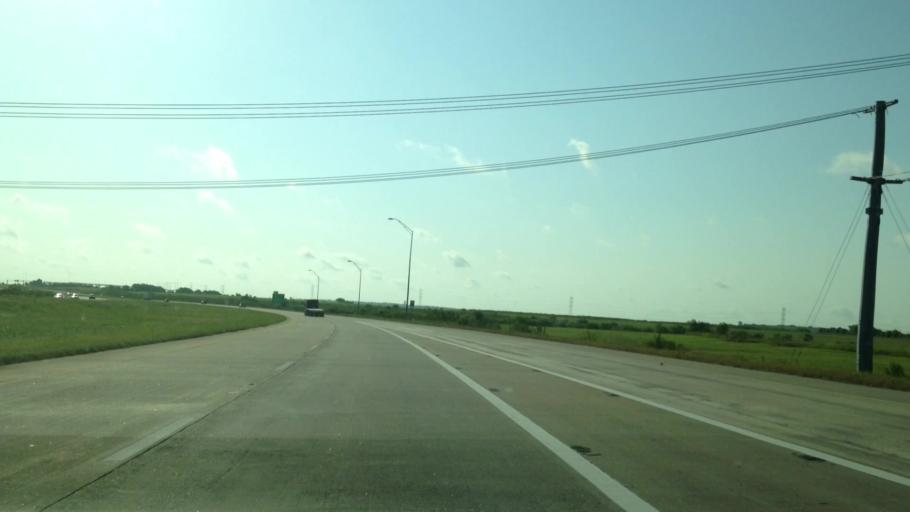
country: US
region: Texas
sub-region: Travis County
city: Onion Creek
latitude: 30.0814
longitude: -97.7306
